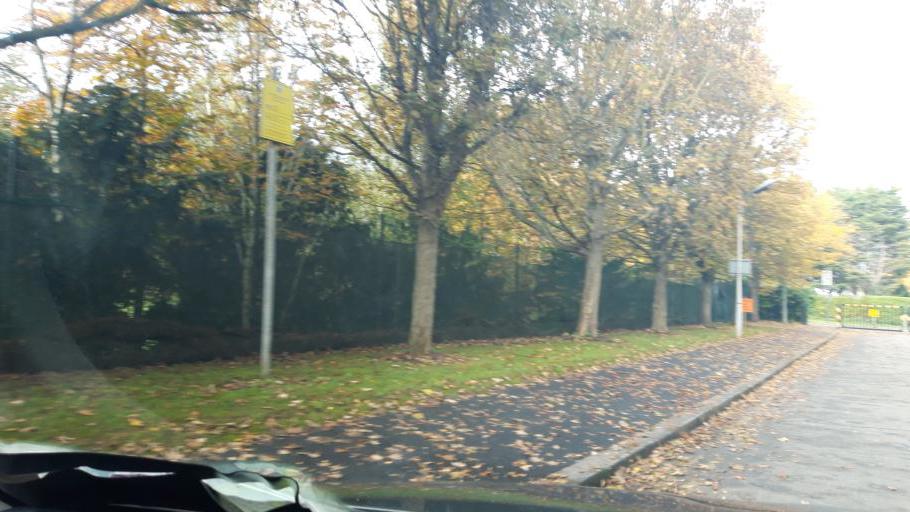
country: IE
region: Leinster
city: Donnybrook
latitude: 53.3110
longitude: -6.2271
